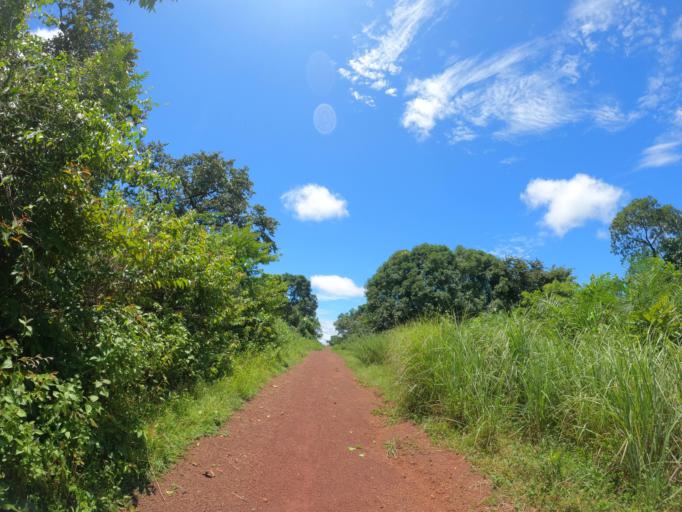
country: SL
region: Northern Province
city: Makeni
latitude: 9.0722
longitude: -12.2748
